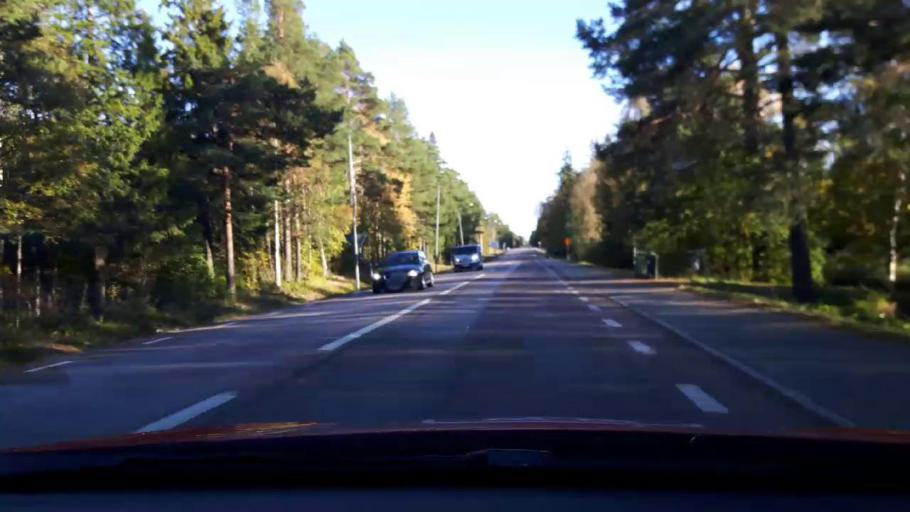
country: SE
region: Jaemtland
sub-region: OEstersunds Kommun
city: Brunflo
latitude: 63.0687
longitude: 14.8440
